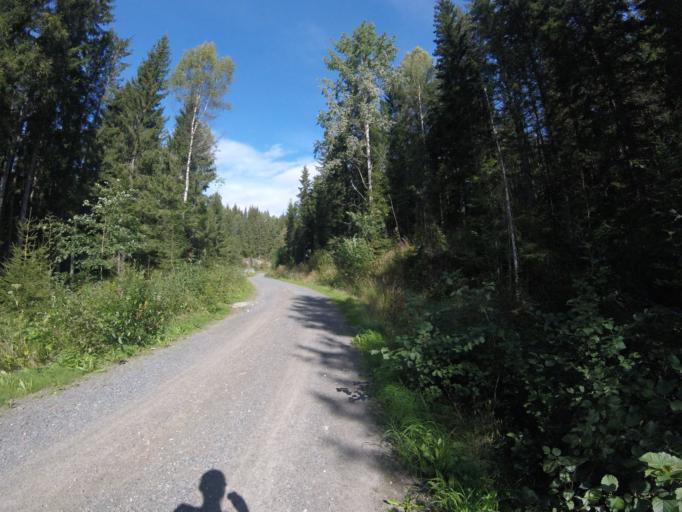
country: NO
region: Akershus
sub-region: Lorenskog
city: Kjenn
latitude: 59.8578
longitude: 10.9977
